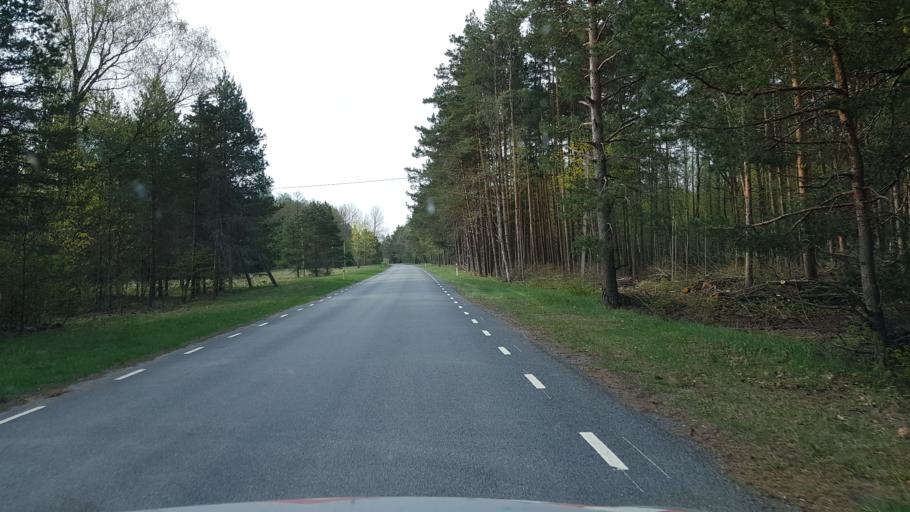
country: EE
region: Paernumaa
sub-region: Audru vald
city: Audru
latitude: 58.3562
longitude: 24.2566
